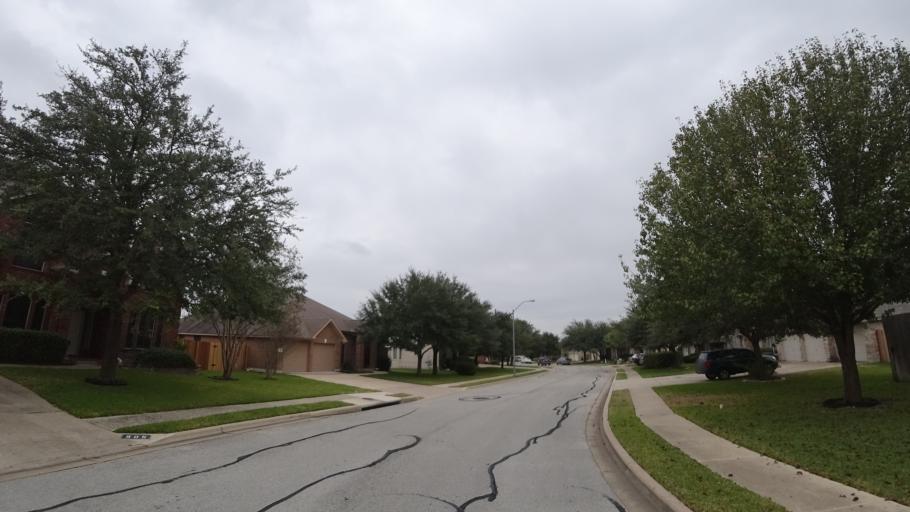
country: US
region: Texas
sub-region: Travis County
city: Pflugerville
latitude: 30.4294
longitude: -97.6174
